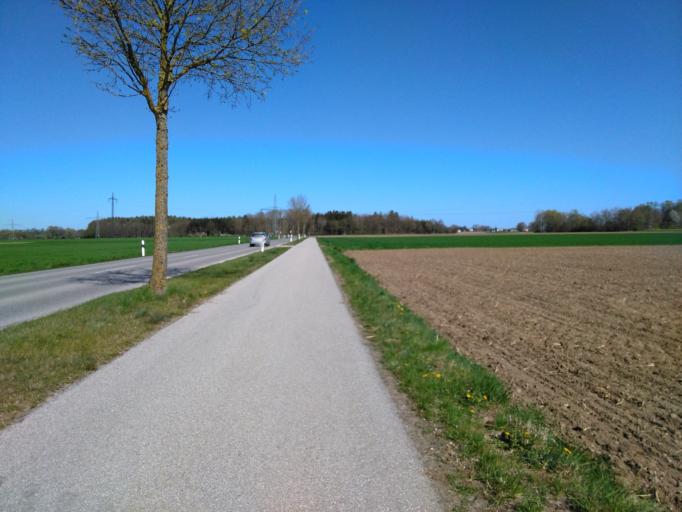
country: DE
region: Bavaria
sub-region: Upper Bavaria
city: Mammendorf
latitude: 48.2105
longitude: 11.1848
